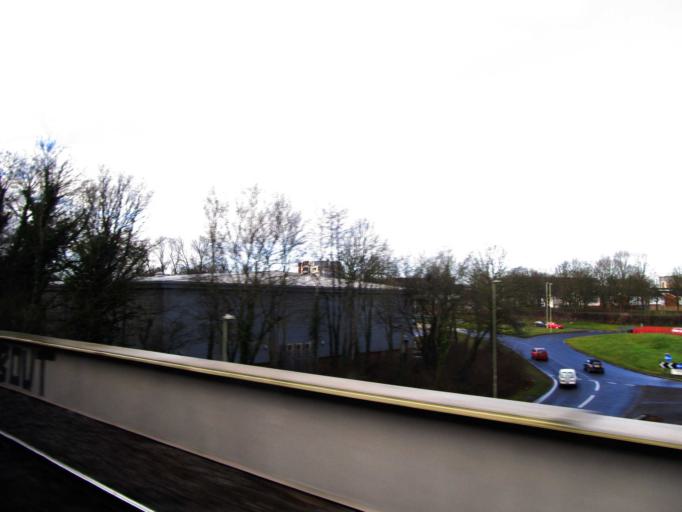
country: GB
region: England
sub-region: Hampshire
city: Basingstoke
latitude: 51.2850
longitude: -1.0687
